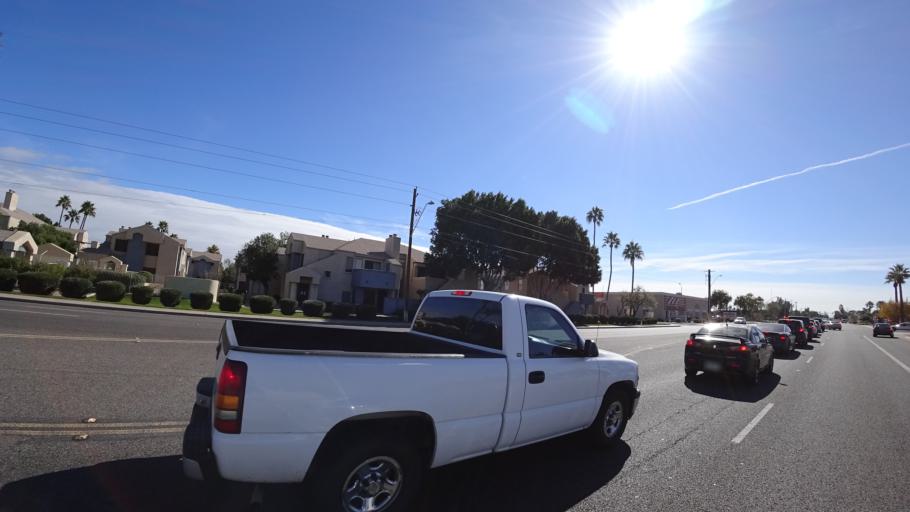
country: US
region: Arizona
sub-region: Maricopa County
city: Glendale
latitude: 33.5706
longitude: -112.1864
